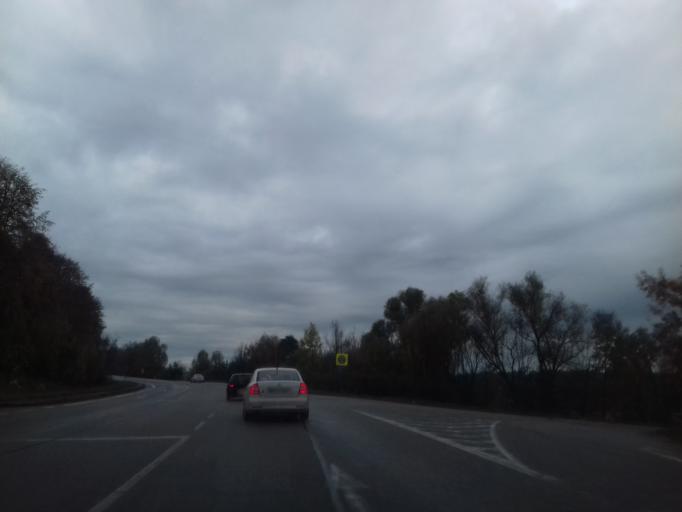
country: CZ
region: Pardubicky
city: Horni Jeleni
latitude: 50.0018
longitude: 16.1015
